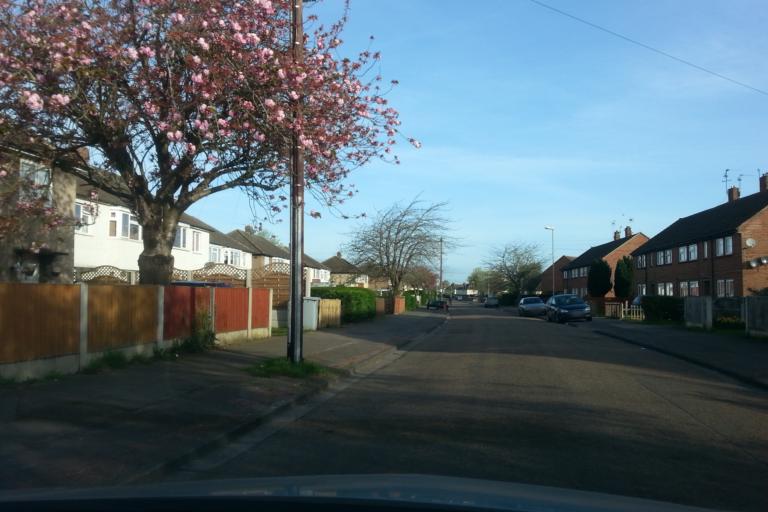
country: GB
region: England
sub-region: Nottinghamshire
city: Newark on Trent
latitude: 53.0604
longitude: -0.8154
